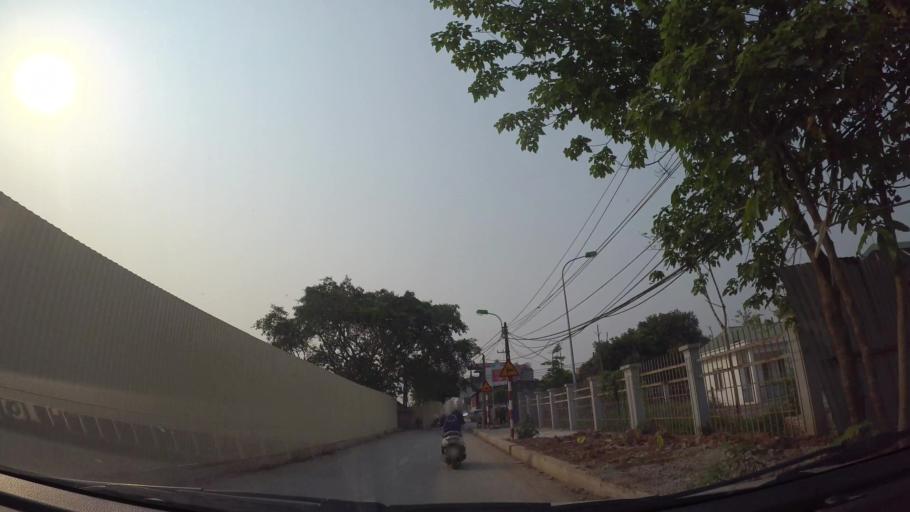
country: VN
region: Ha Noi
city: Ha Dong
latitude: 20.9987
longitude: 105.7425
